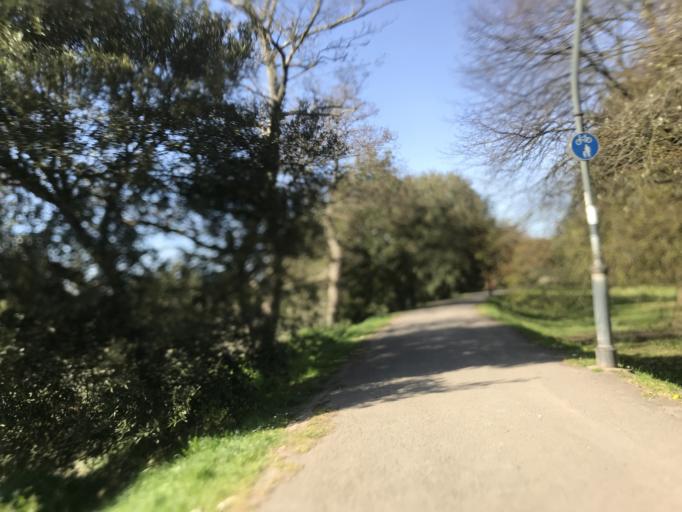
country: GB
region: England
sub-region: Devon
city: Barnstaple
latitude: 51.0687
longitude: -4.0561
